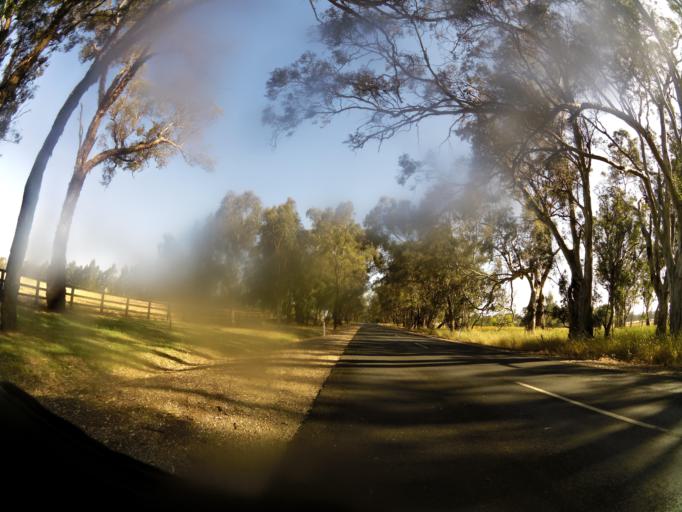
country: AU
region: Victoria
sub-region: Murrindindi
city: Kinglake West
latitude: -36.9573
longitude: 145.1073
